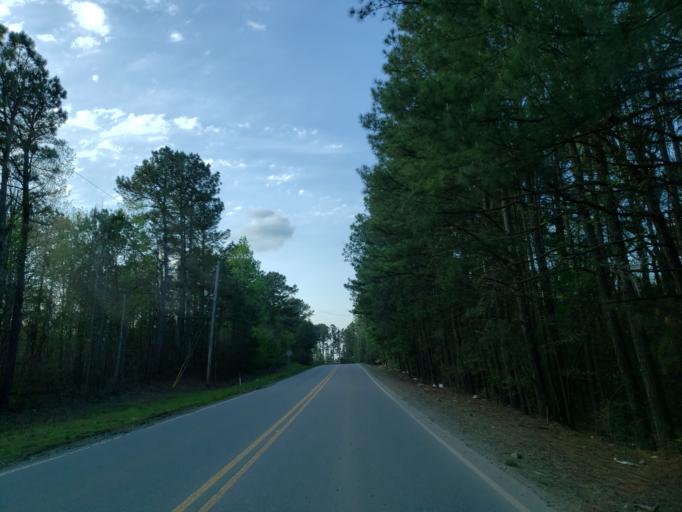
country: US
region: Georgia
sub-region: Cherokee County
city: Ball Ground
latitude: 34.2898
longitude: -84.3856
